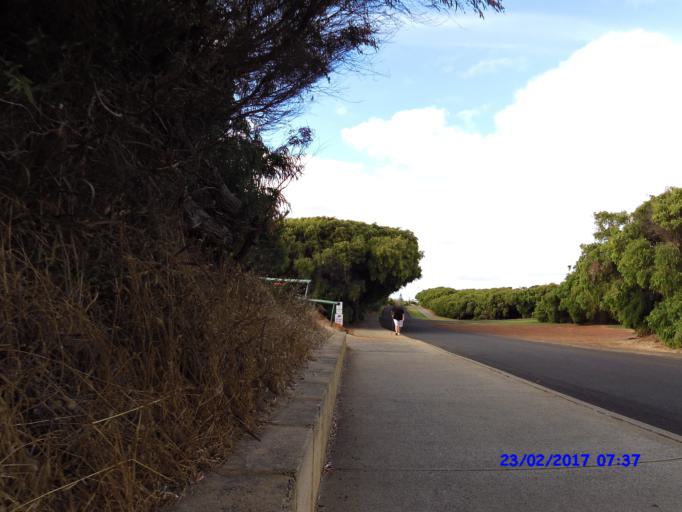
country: AU
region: Western Australia
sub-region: Augusta-Margaret River Shire
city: Augusta
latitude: -34.3267
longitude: 115.1701
